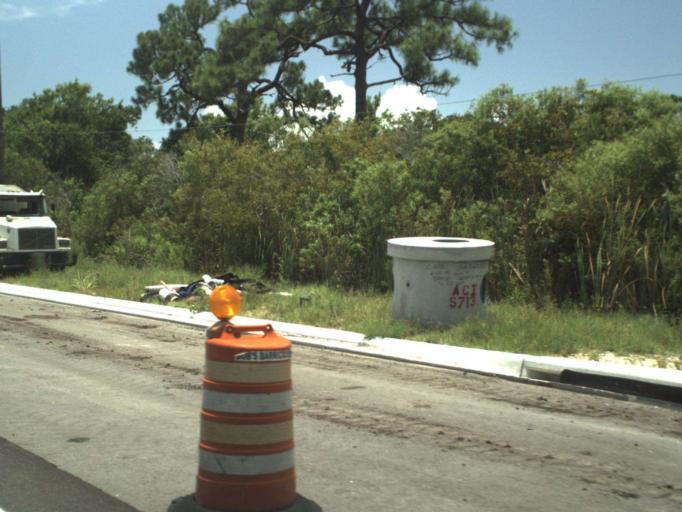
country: US
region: Florida
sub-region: Indian River County
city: Florida Ridge
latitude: 27.5763
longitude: -80.3748
